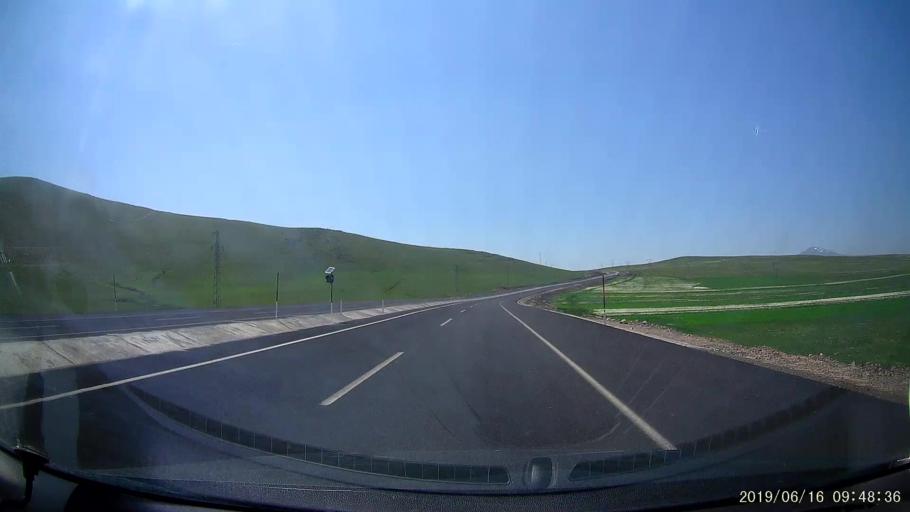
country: TR
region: Kars
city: Digor
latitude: 40.4317
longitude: 43.3544
